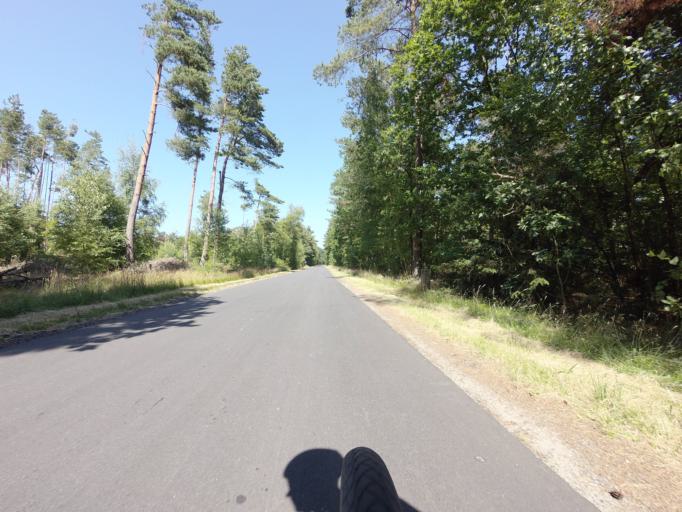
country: DK
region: North Denmark
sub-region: Laeso Kommune
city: Byrum
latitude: 57.2672
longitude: 11.0044
